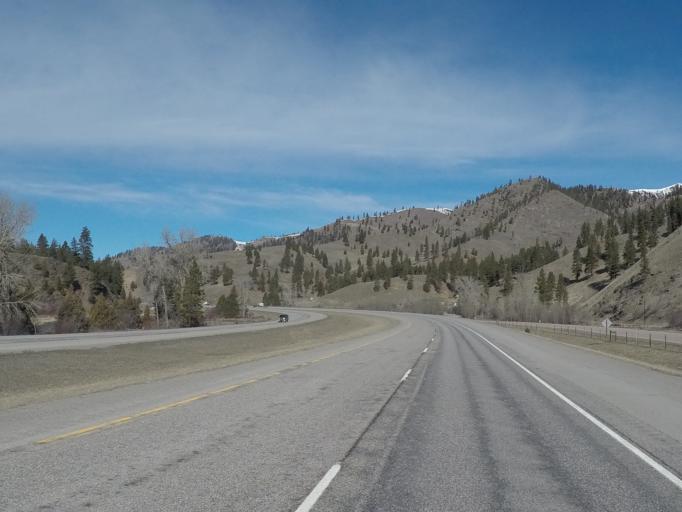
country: US
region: Montana
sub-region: Missoula County
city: Clinton
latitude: 46.7082
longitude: -113.5068
